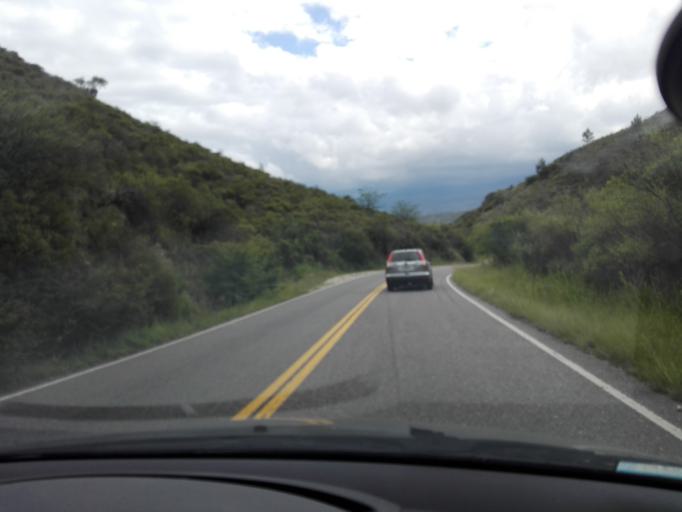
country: AR
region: Cordoba
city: Cuesta Blanca
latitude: -31.6035
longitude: -64.5510
